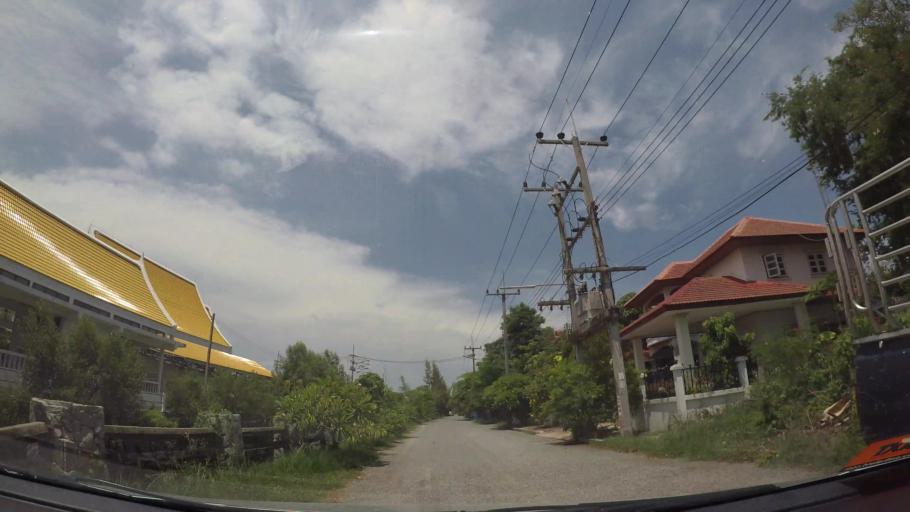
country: TH
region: Chon Buri
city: Chon Buri
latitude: 13.3325
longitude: 100.9412
